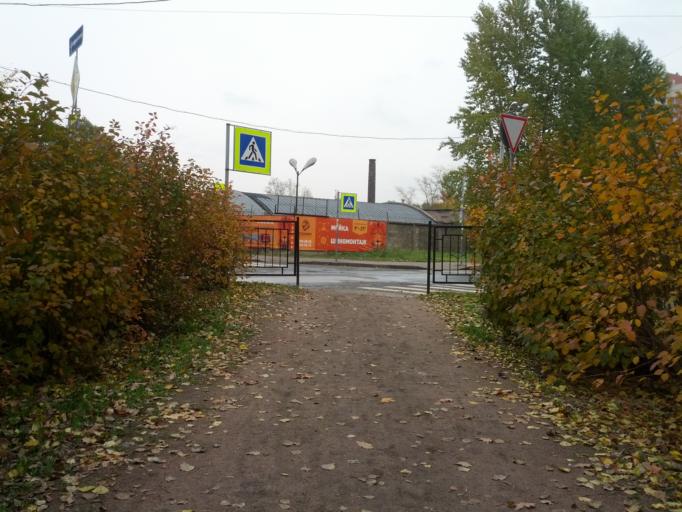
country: RU
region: St.-Petersburg
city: Obukhovo
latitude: 59.8931
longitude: 30.4195
